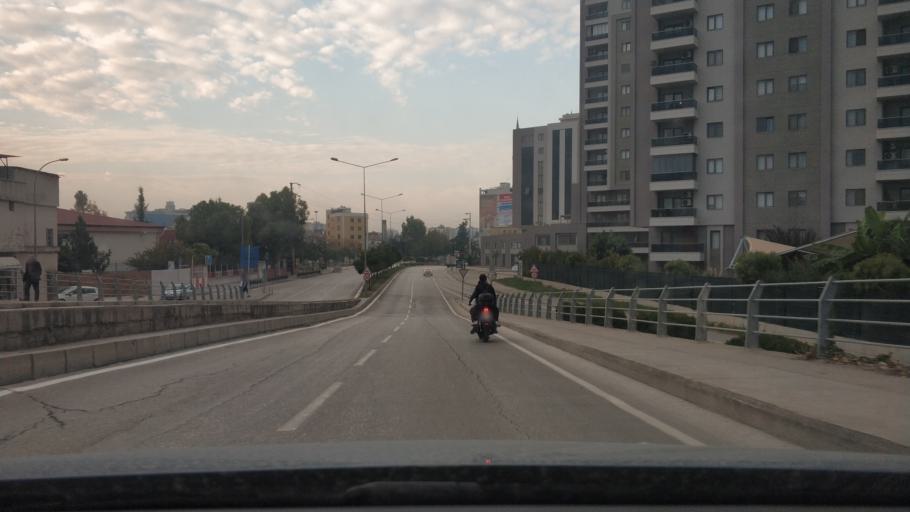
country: TR
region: Adana
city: Adana
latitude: 36.9932
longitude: 35.3200
